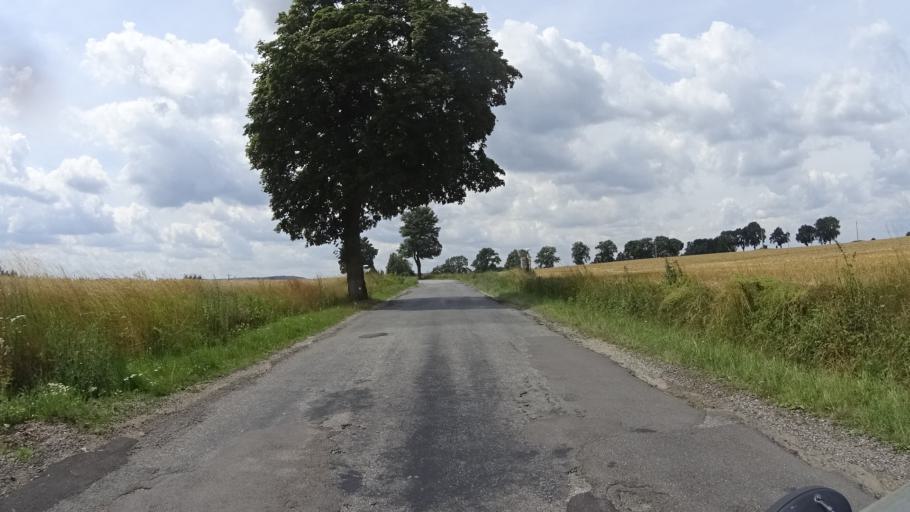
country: CZ
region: Vysocina
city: Merin
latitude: 49.4032
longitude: 15.9174
